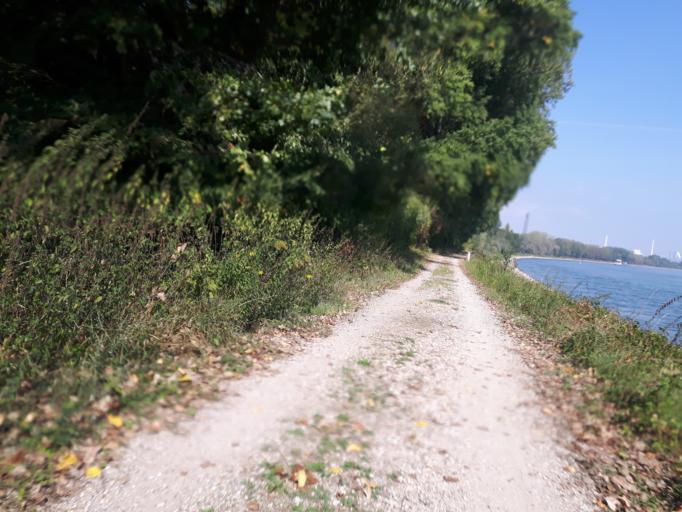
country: DE
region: Rheinland-Pfalz
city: Altrip
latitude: 49.3989
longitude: 8.4955
